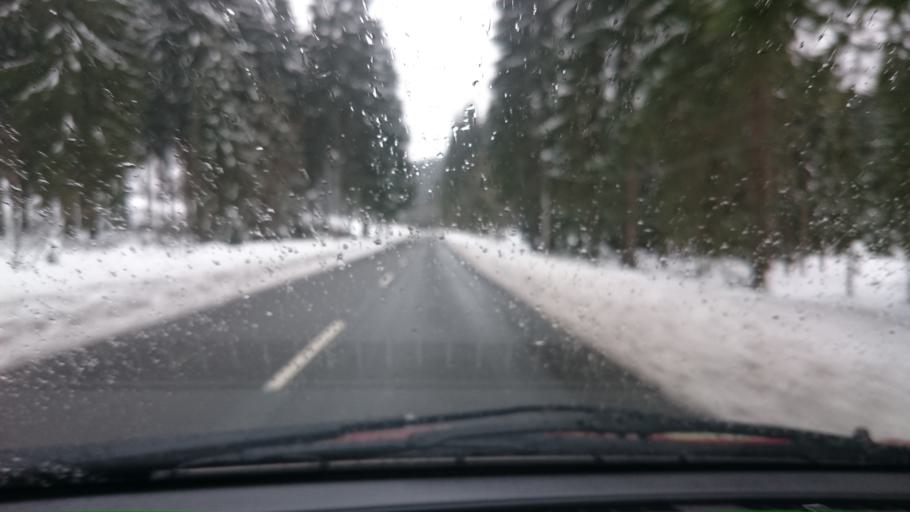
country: DE
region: Saxony
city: Tannenbergsthal
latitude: 50.4142
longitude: 12.4841
